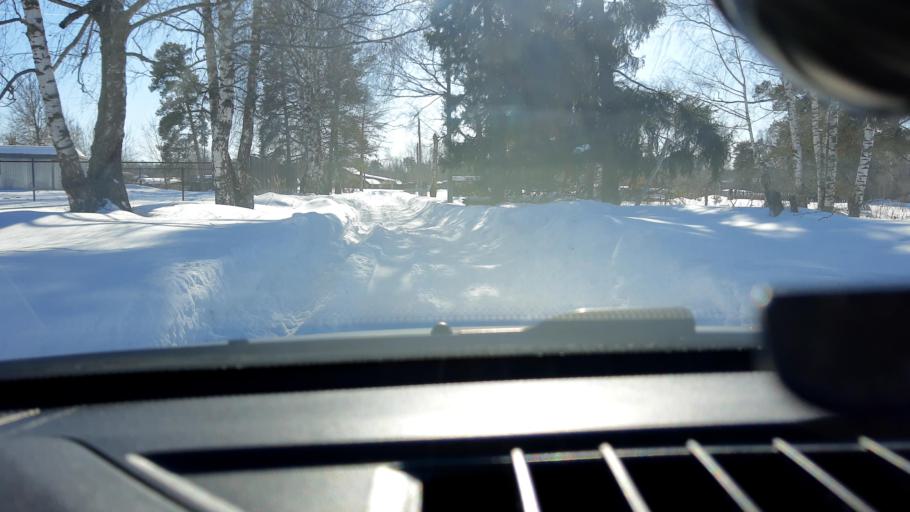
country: RU
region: Nizjnij Novgorod
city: Yuganets
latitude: 56.2558
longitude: 43.2259
